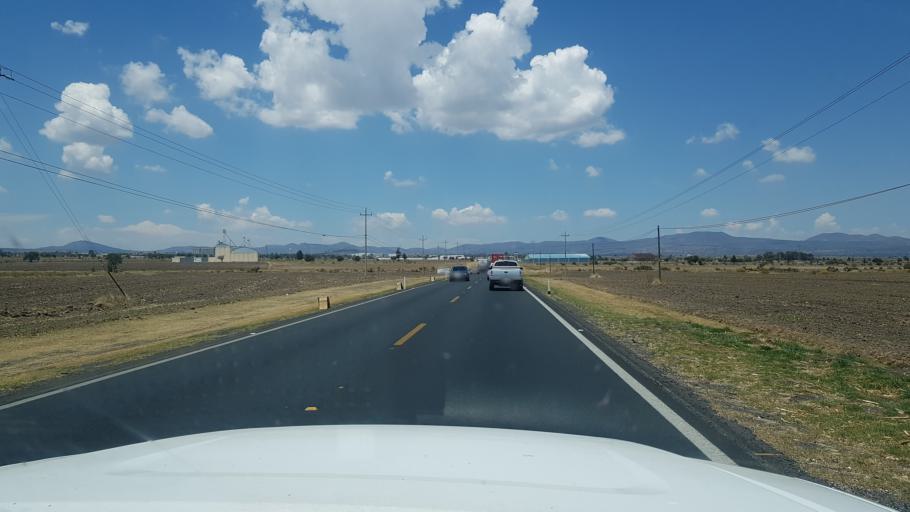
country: MX
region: Hidalgo
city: Calpulalpan
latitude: 19.5778
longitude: -98.5211
